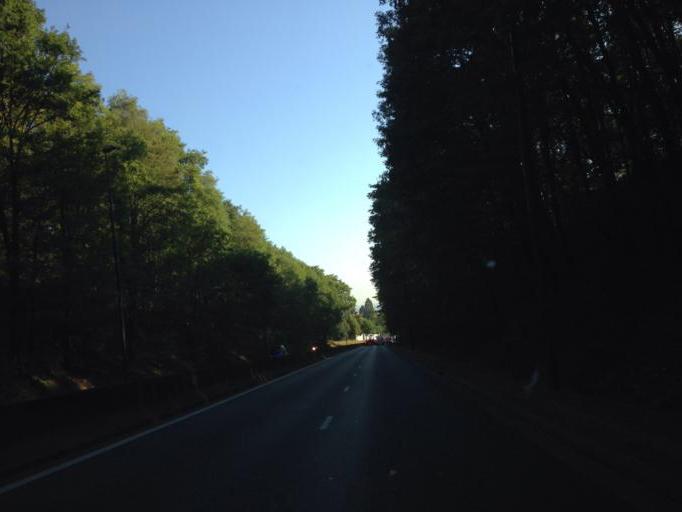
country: FR
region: Ile-de-France
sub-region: Departement des Hauts-de-Seine
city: Clamart
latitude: 48.8008
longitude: 2.2550
